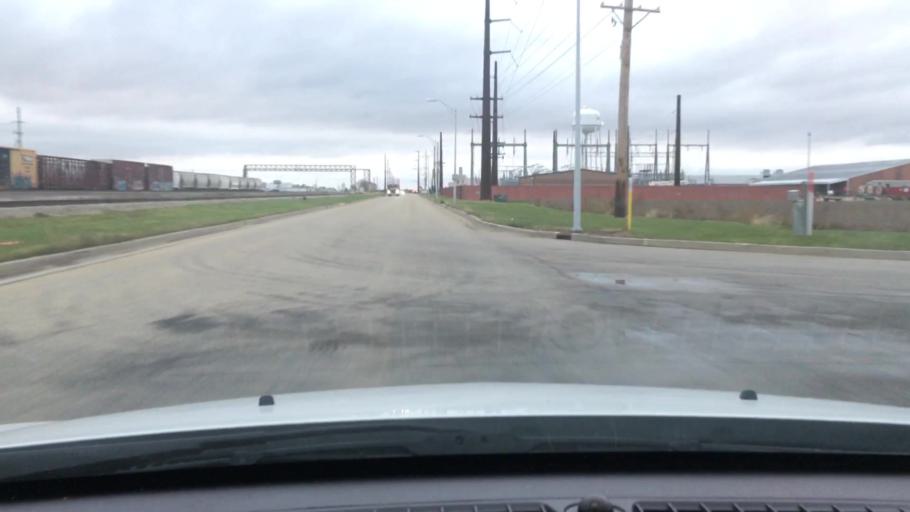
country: US
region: Illinois
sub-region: Ogle County
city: Rochelle
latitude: 41.9041
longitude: -89.0450
